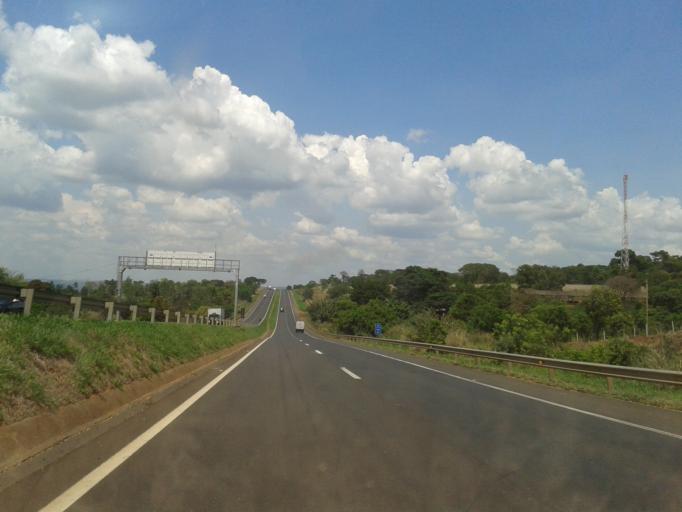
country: BR
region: Minas Gerais
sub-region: Araguari
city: Araguari
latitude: -18.7063
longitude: -48.1916
